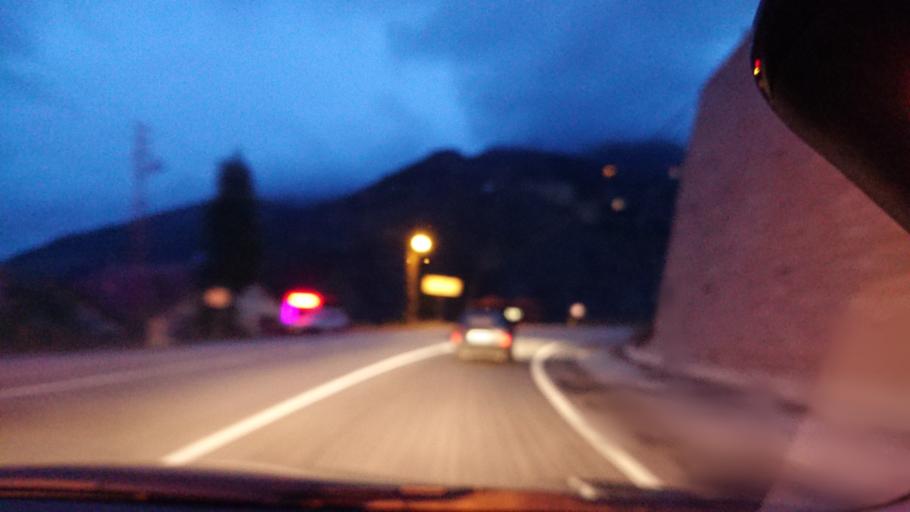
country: TR
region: Gumushane
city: Kurtun
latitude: 40.6727
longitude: 39.1381
